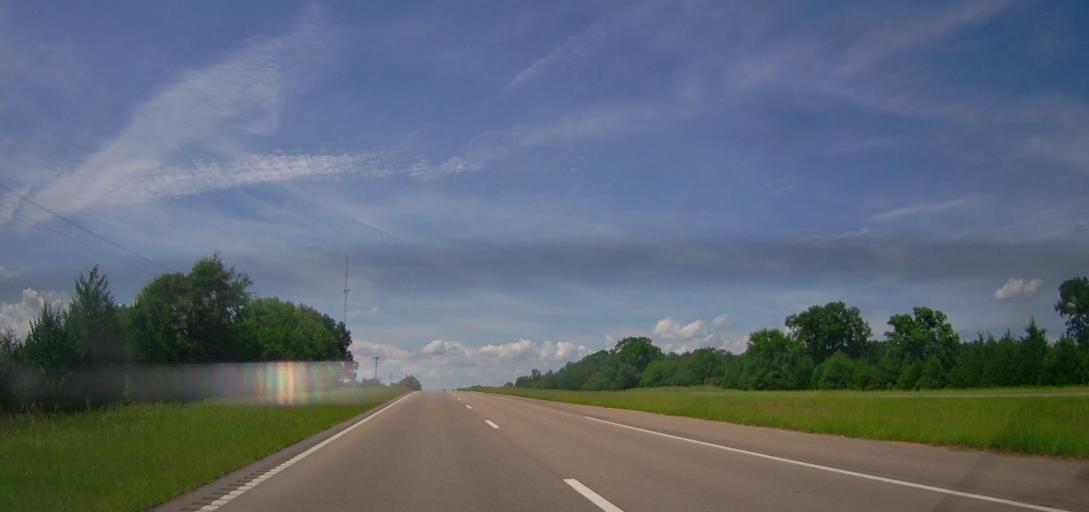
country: US
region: Mississippi
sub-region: Monroe County
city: Amory
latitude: 33.9472
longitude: -88.6017
